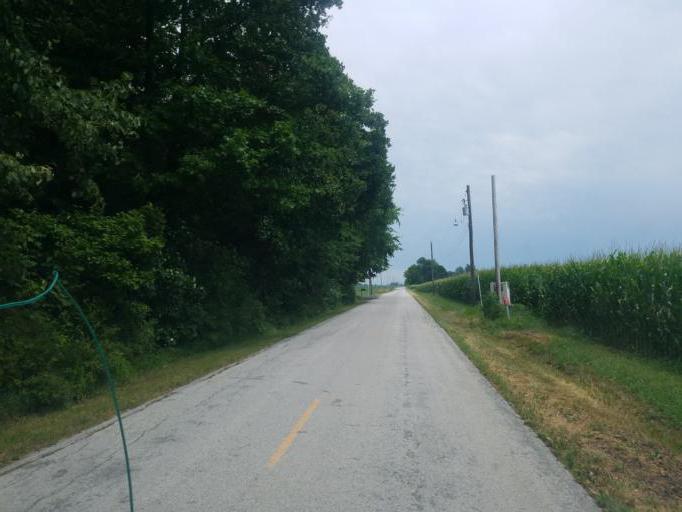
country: US
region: Ohio
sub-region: Defiance County
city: Hicksville
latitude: 41.2372
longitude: -84.7693
